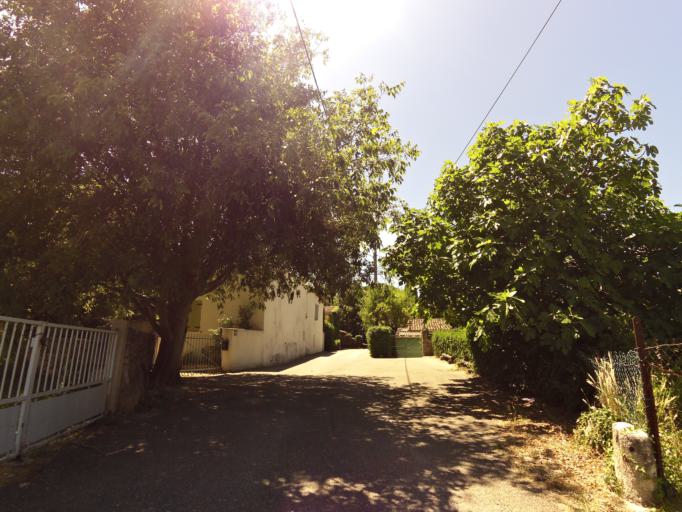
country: FR
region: Languedoc-Roussillon
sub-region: Departement du Gard
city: Aigues-Vives
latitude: 43.7389
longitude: 4.1692
